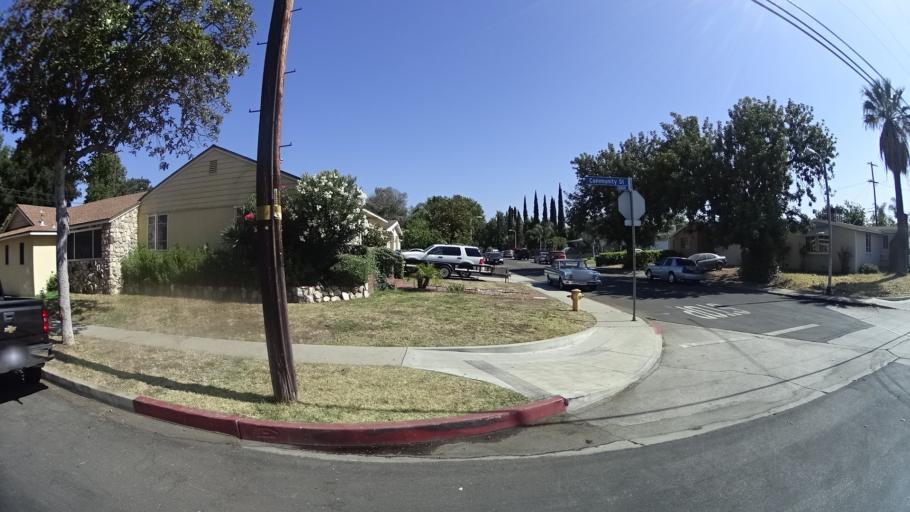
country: US
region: California
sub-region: Los Angeles County
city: Van Nuys
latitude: 34.2226
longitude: -118.4342
